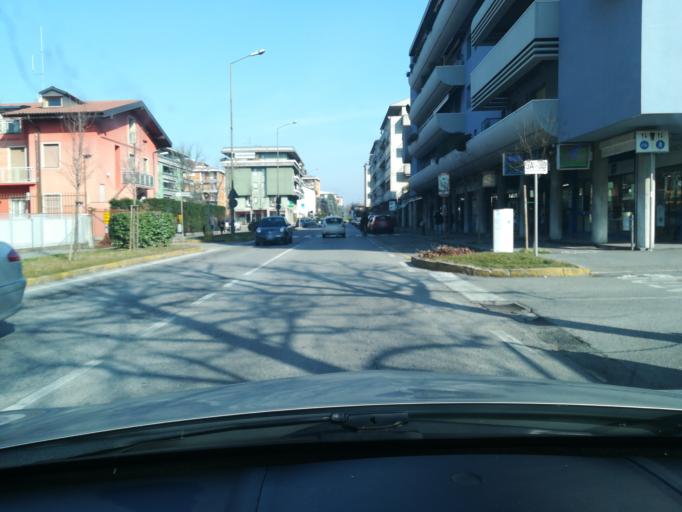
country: IT
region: Lombardy
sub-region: Provincia di Bergamo
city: Stezzano
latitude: 45.6525
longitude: 9.6498
